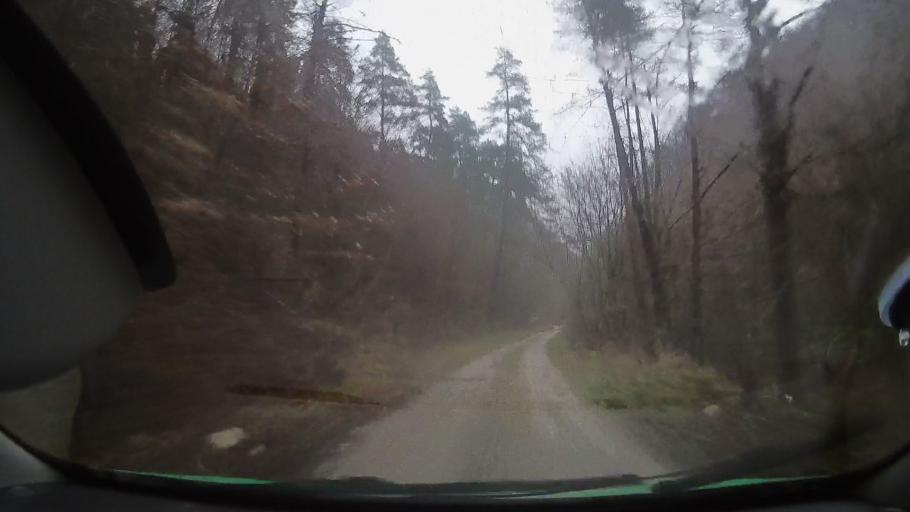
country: RO
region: Alba
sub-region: Comuna Avram Iancu
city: Avram Iancu
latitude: 46.3074
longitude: 22.7691
